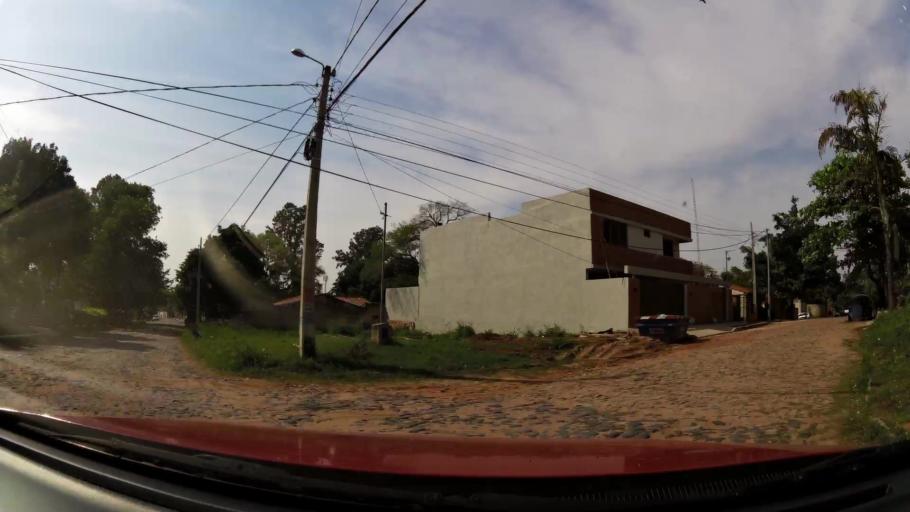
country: PY
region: Central
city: Fernando de la Mora
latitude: -25.2613
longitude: -57.5516
